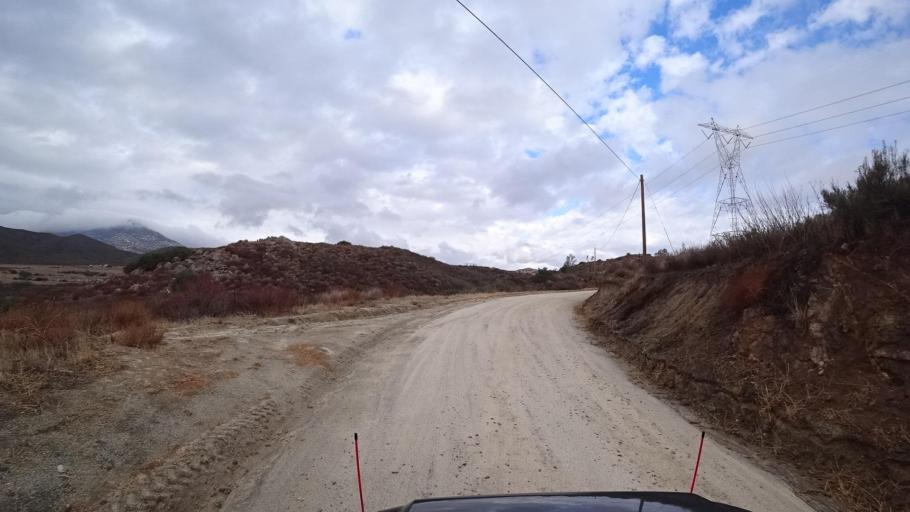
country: MX
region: Baja California
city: Tecate
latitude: 32.5951
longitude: -116.6348
